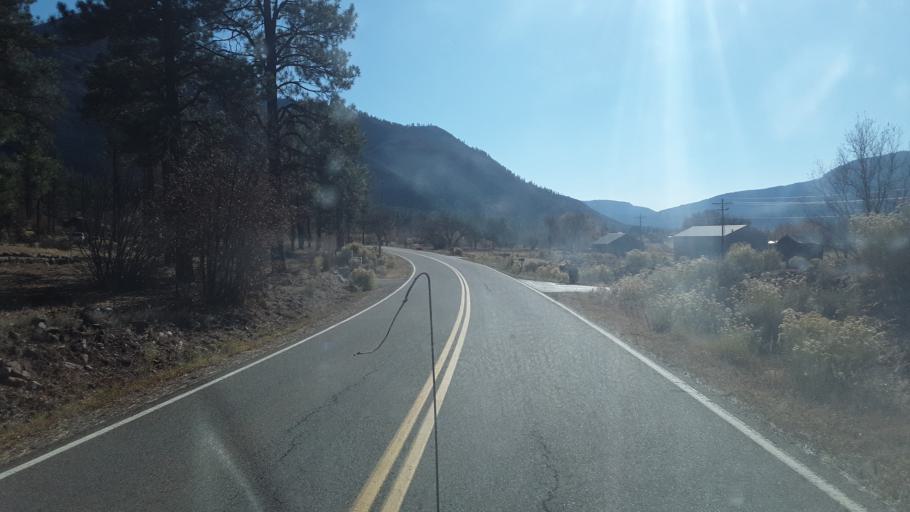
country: US
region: Colorado
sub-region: La Plata County
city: Durango
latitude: 37.4094
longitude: -107.8132
